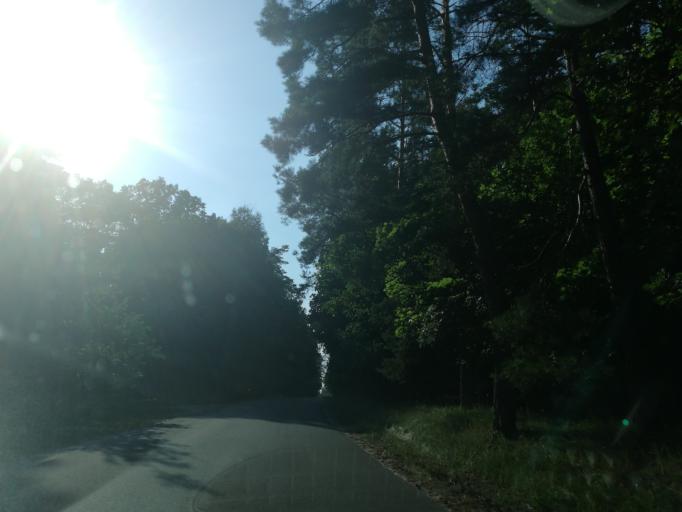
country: PL
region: Kujawsko-Pomorskie
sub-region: Powiat golubsko-dobrzynski
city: Ciechocin
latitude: 53.0975
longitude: 18.9355
